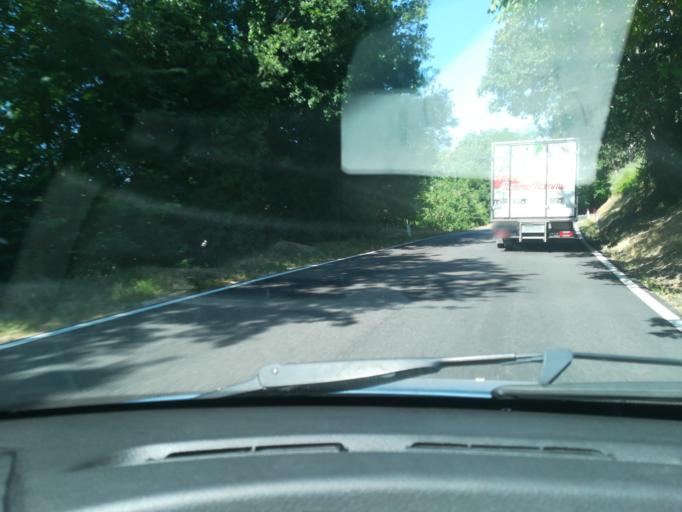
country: IT
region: The Marches
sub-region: Provincia di Macerata
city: Ripe San Ginesio
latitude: 43.1125
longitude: 13.3647
